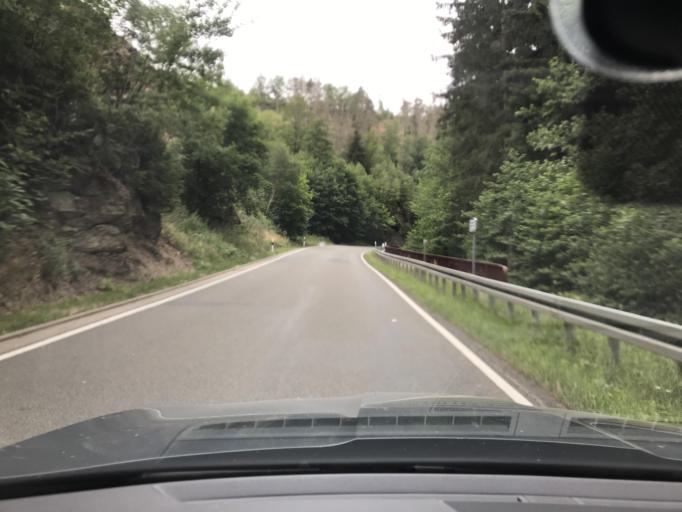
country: DE
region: Saxony-Anhalt
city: Harzgerode
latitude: 51.6386
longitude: 11.1040
